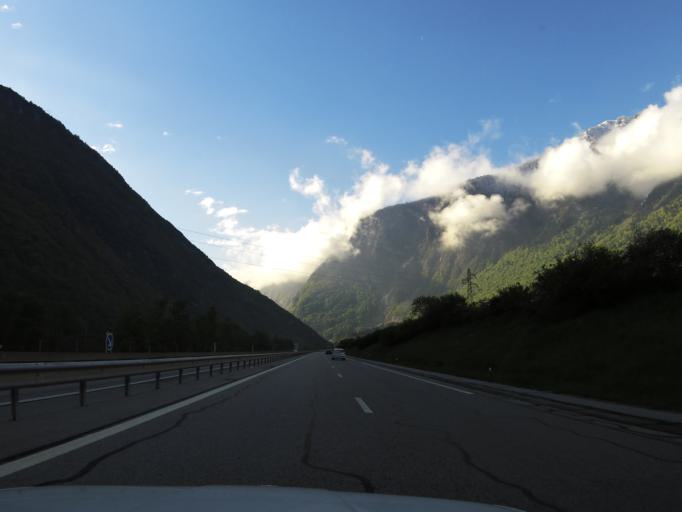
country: FR
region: Rhone-Alpes
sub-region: Departement de la Savoie
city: La Chambre
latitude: 45.3316
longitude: 6.3146
